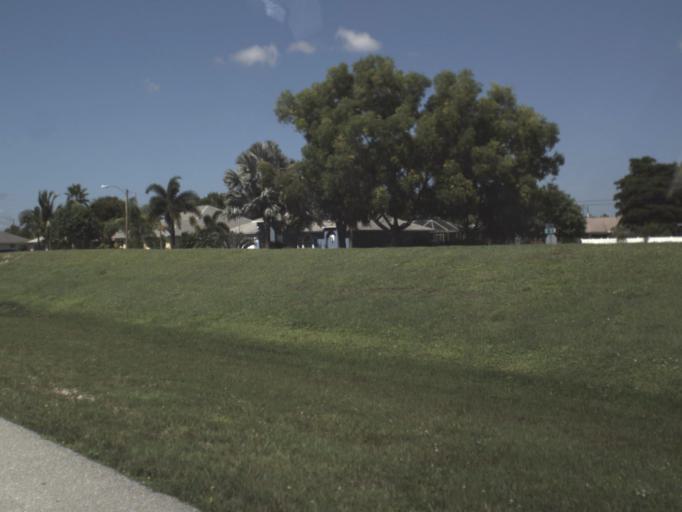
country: US
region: Florida
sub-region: Lee County
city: Cape Coral
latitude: 26.6045
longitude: -81.9701
